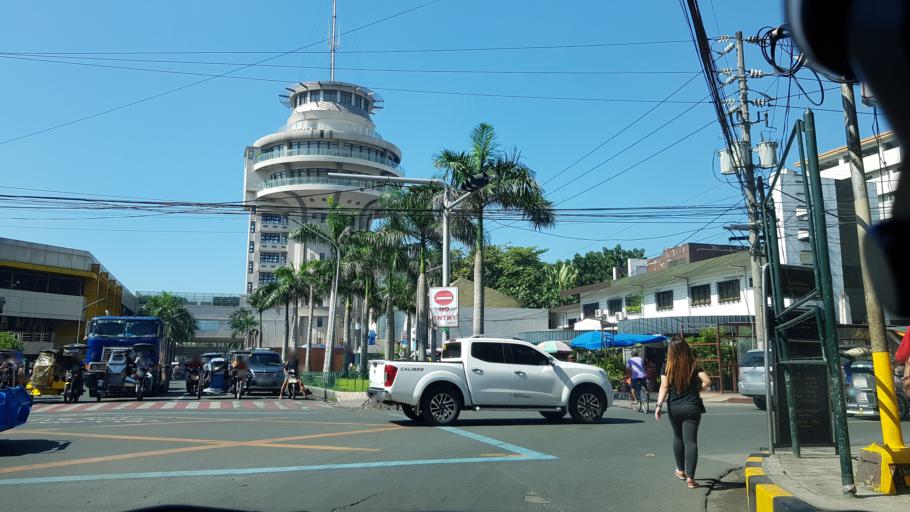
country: PH
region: Calabarzon
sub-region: Province of Rizal
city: Pateros
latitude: 14.5598
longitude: 121.0837
